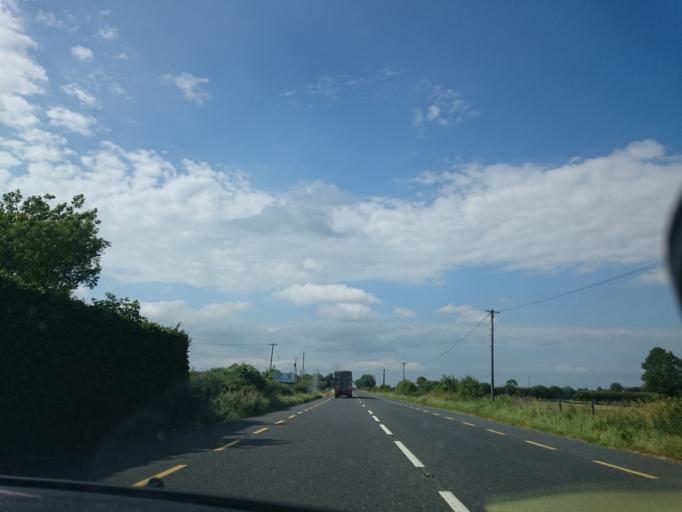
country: IE
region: Leinster
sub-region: Kilkenny
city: Kilkenny
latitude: 52.6096
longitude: -7.2441
